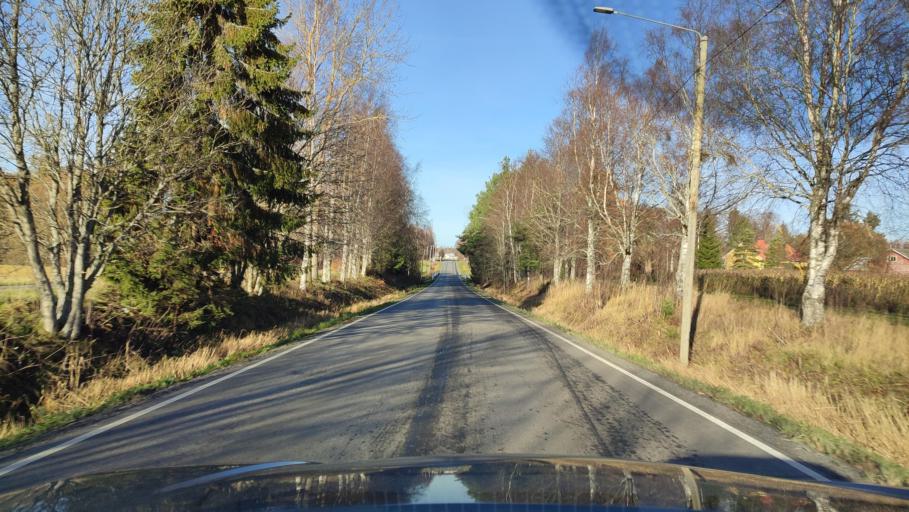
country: FI
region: Southern Ostrobothnia
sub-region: Suupohja
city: Karijoki
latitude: 62.3004
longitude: 21.7178
